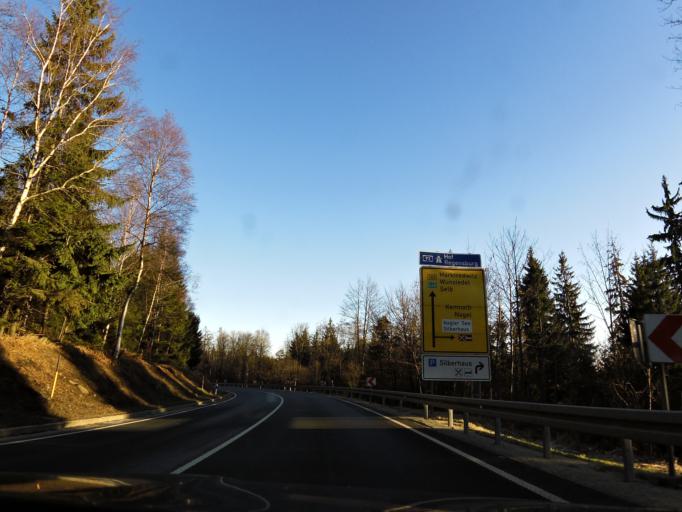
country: DE
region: Bavaria
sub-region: Upper Franconia
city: Nagel
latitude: 50.0049
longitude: 11.8925
